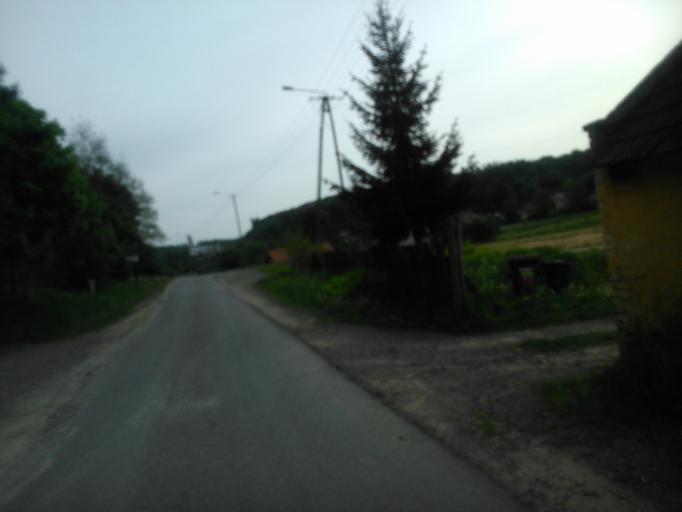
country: PL
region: Swietokrzyskie
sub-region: Powiat ostrowiecki
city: Baltow
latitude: 51.0144
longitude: 21.5421
